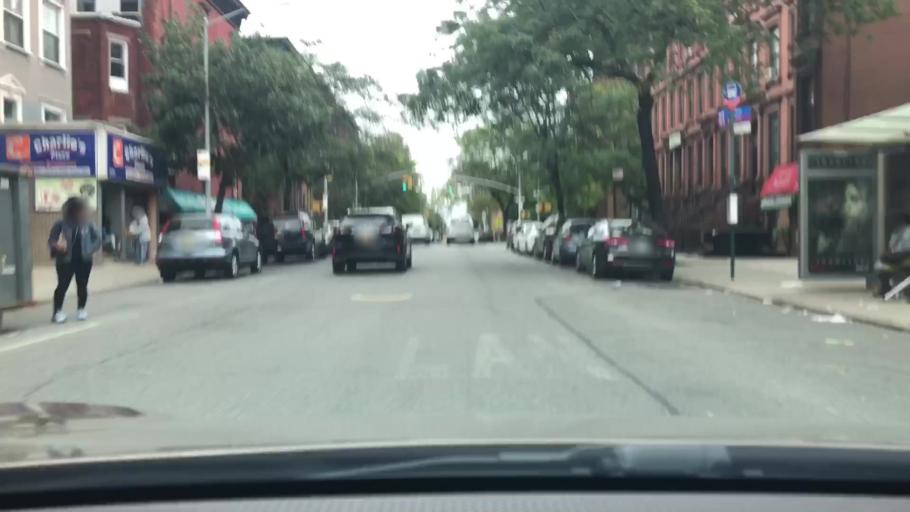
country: US
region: New York
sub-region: New York County
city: Manhattan
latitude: 40.8060
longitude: -73.9405
